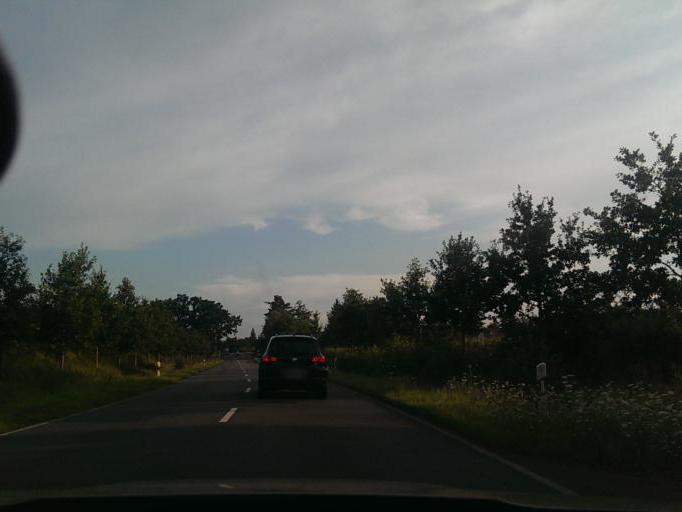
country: DE
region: Lower Saxony
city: Lilienthal
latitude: 53.1369
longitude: 8.8944
